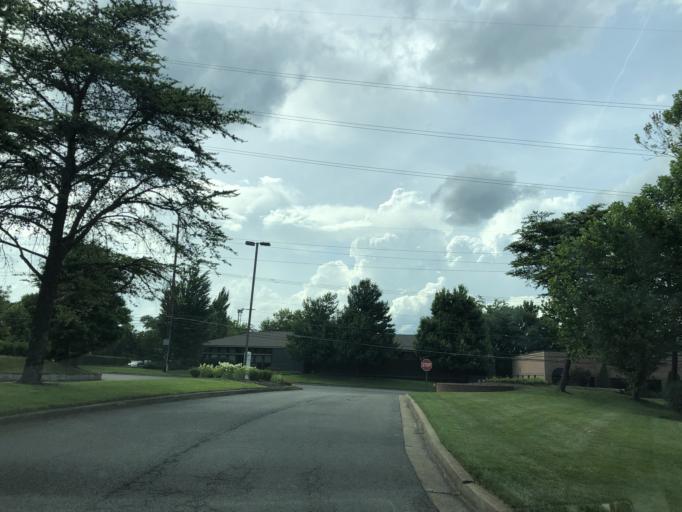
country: US
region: Tennessee
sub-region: Davidson County
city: Oak Hill
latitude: 36.0867
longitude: -86.7528
